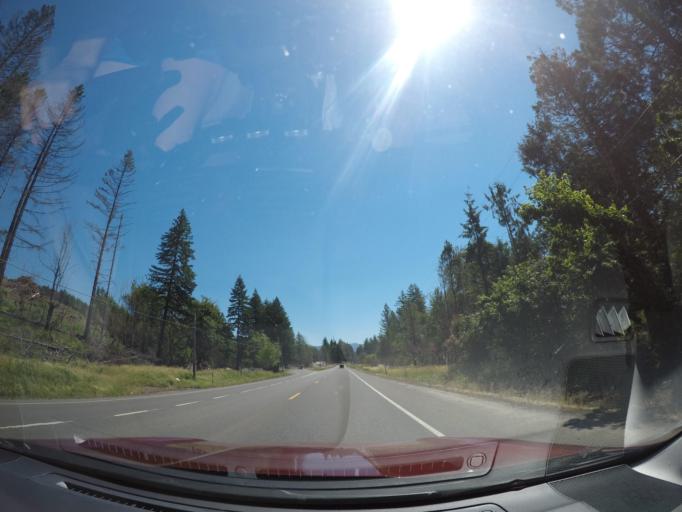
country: US
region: Oregon
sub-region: Linn County
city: Mill City
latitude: 44.7569
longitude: -122.4405
